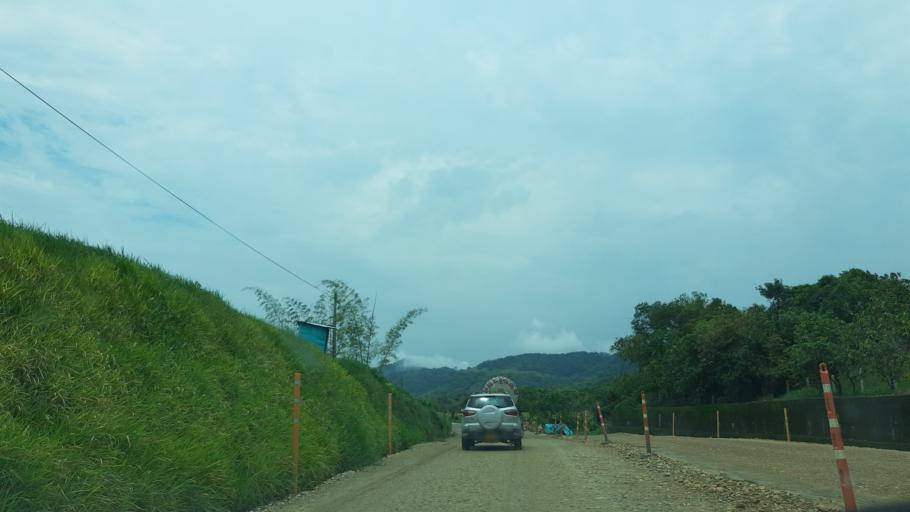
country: CO
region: Casanare
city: Sabanalarga
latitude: 4.7821
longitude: -72.9988
